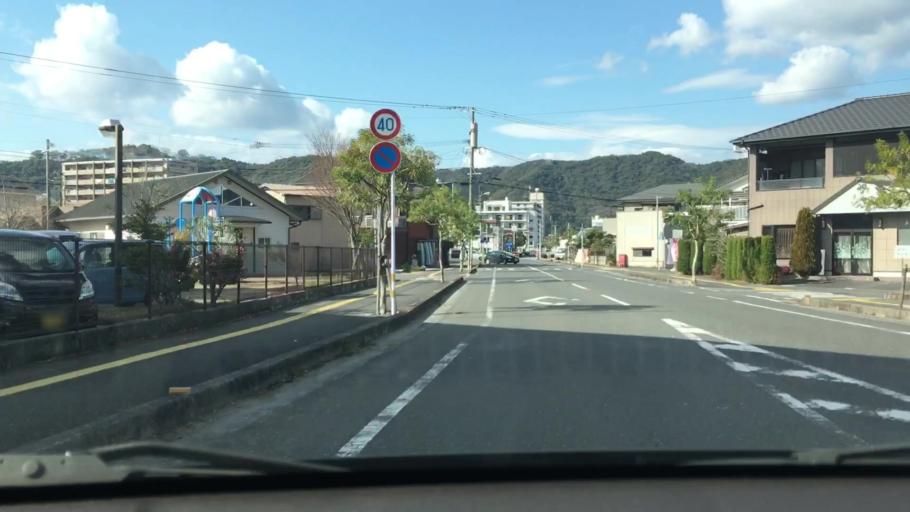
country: JP
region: Oita
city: Saiki
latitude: 32.9588
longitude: 131.9044
